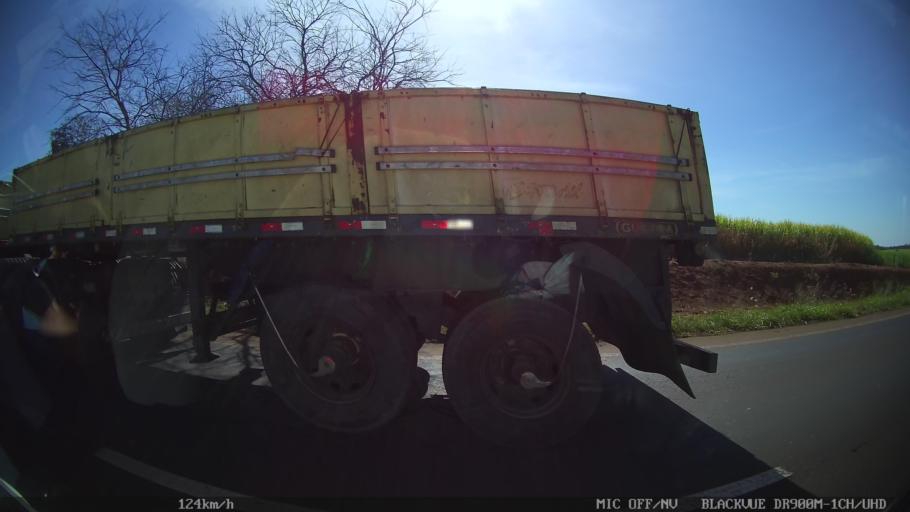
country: BR
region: Sao Paulo
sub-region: Barretos
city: Barretos
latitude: -20.5639
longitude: -48.6583
